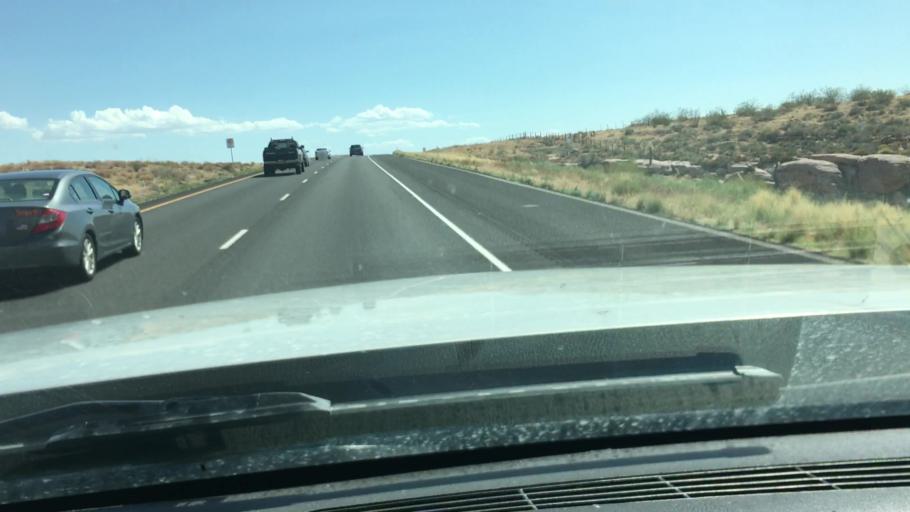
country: US
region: Utah
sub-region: Washington County
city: Washington
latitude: 37.1864
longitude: -113.4120
